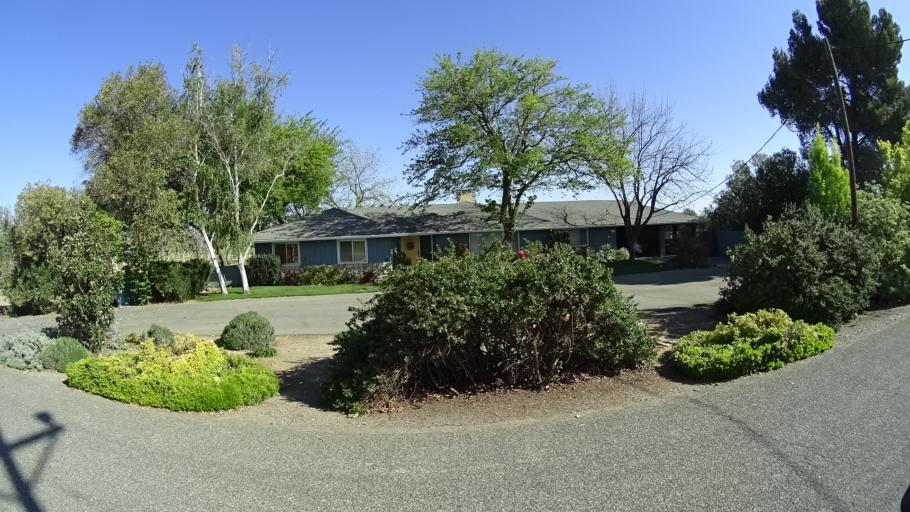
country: US
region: California
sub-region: Glenn County
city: Orland
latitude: 39.7541
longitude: -122.1480
